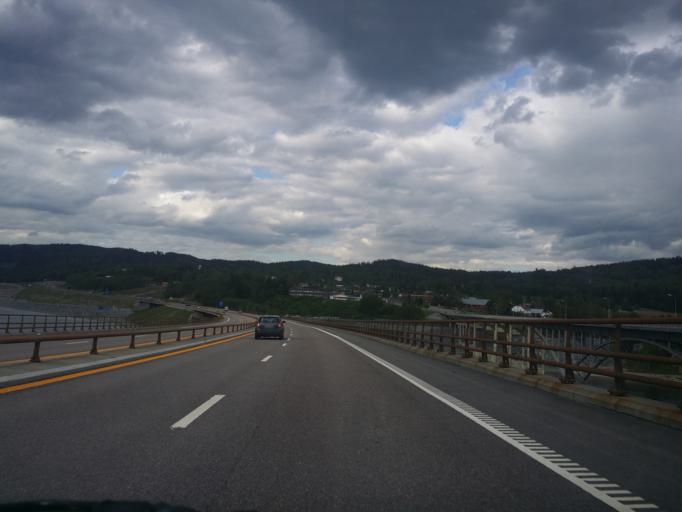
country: NO
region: Akershus
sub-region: Eidsvoll
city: Eidsvoll
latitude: 60.3981
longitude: 11.2307
